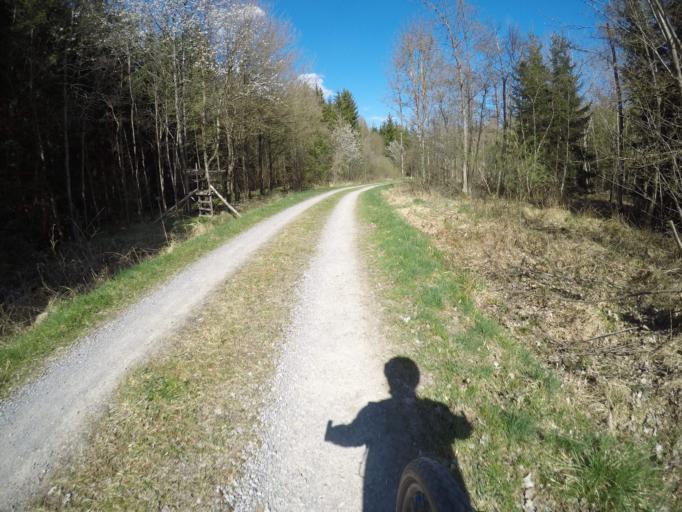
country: DE
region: Baden-Wuerttemberg
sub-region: Regierungsbezirk Stuttgart
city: Altdorf
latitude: 48.6036
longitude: 9.0162
